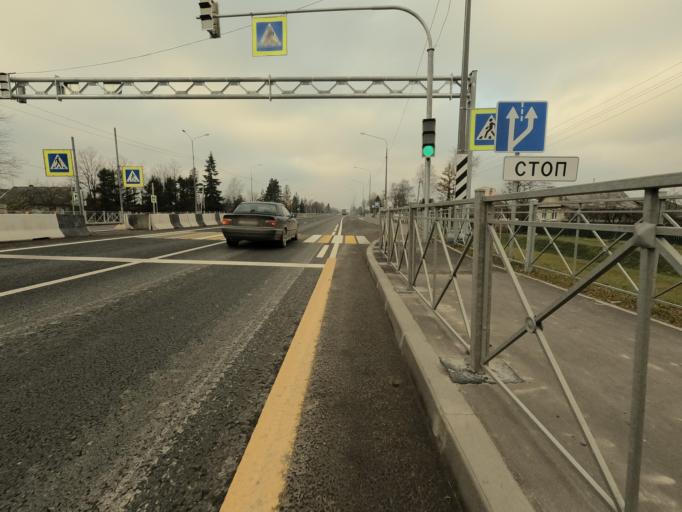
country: RU
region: Leningrad
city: Mga
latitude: 59.7169
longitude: 31.1096
